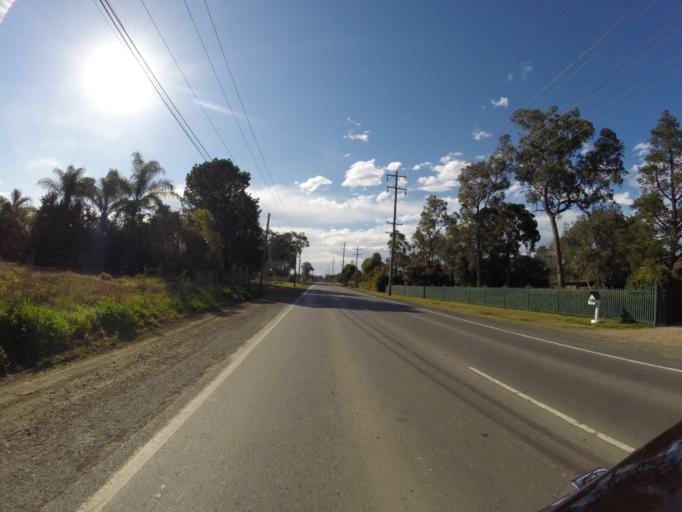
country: AU
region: New South Wales
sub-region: Fairfield
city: Cecil Park
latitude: -33.8892
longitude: 150.7911
